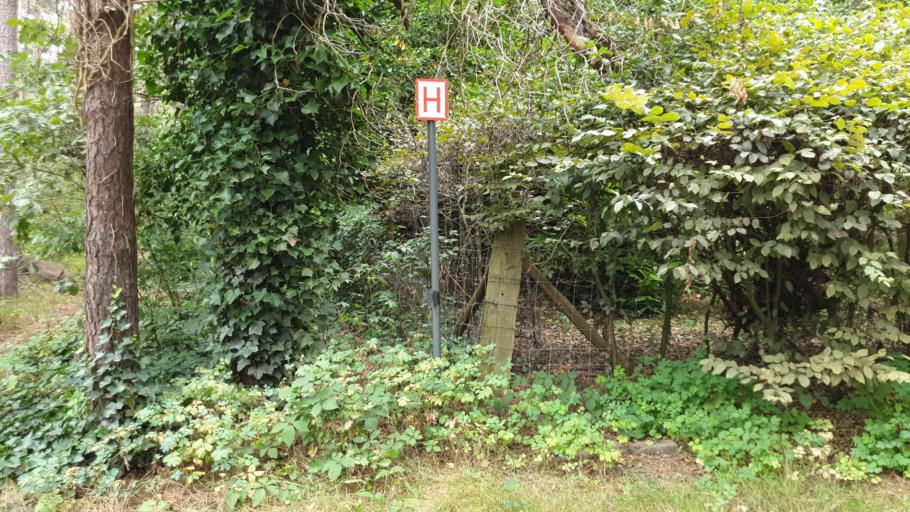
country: BE
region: Flanders
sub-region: Provincie Antwerpen
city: Meerhout
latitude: 51.1438
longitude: 5.0487
